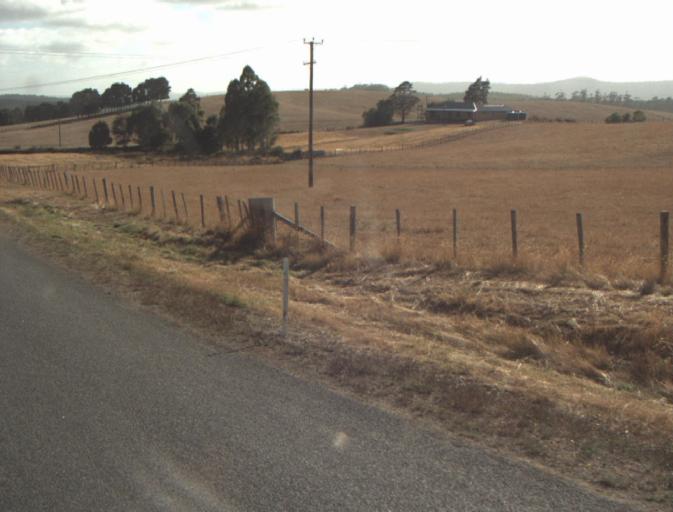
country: AU
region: Tasmania
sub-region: Launceston
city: Mayfield
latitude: -41.1994
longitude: 147.2175
